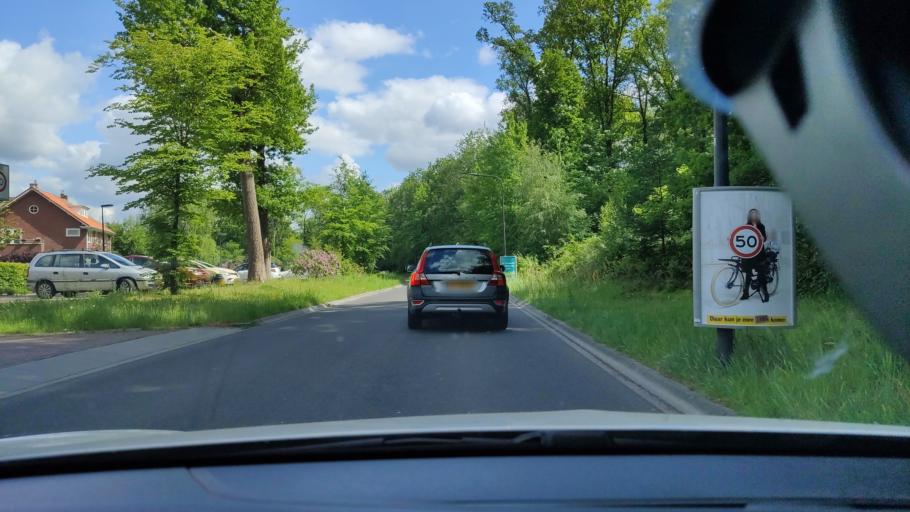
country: NL
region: Drenthe
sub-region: Gemeente Tynaarlo
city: Zuidlaren
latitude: 53.0905
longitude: 6.6785
